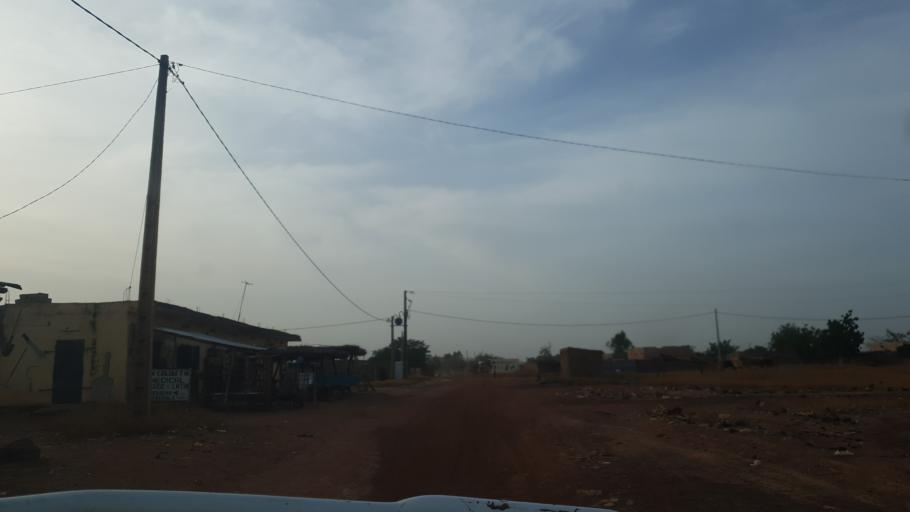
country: ML
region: Segou
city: Baroueli
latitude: 12.7778
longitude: -6.9432
